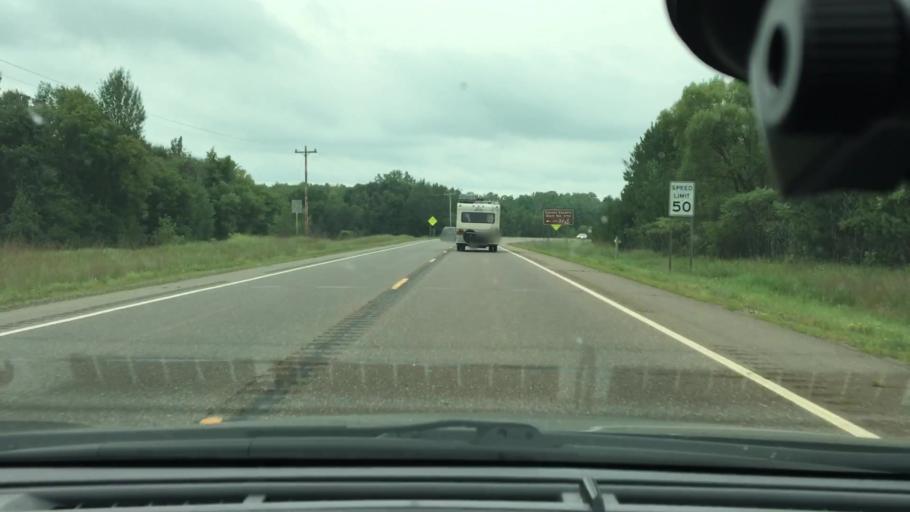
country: US
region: Minnesota
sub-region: Crow Wing County
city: Crosby
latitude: 46.4942
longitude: -93.9562
